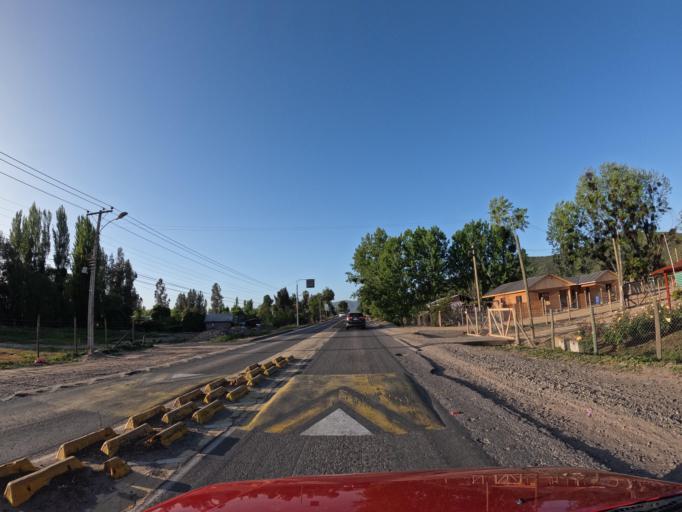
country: CL
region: O'Higgins
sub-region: Provincia de Colchagua
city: Santa Cruz
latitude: -34.4166
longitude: -71.3731
